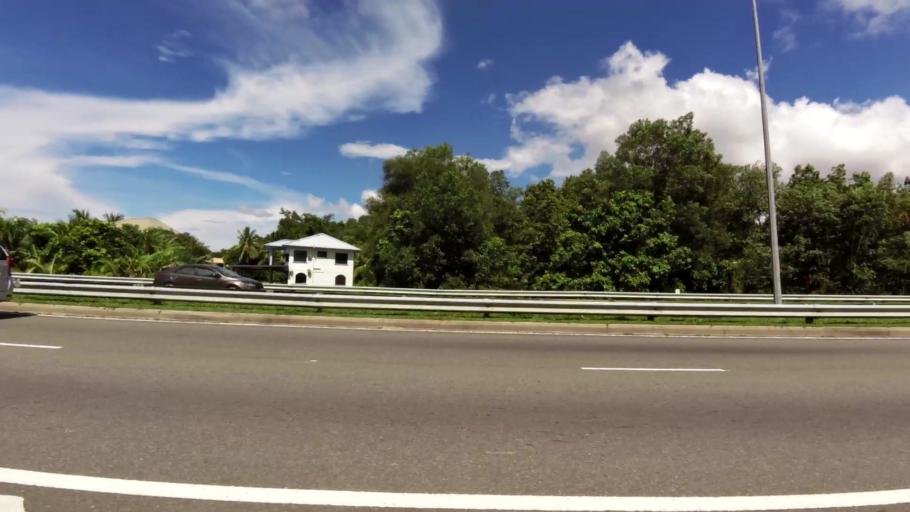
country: BN
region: Brunei and Muara
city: Bandar Seri Begawan
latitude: 4.9748
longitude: 114.9548
